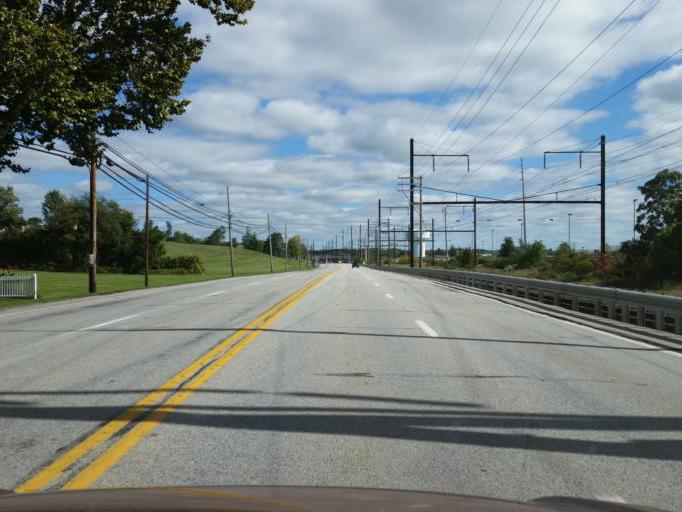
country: US
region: Pennsylvania
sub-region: Dauphin County
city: Middletown
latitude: 40.1976
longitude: -76.7477
